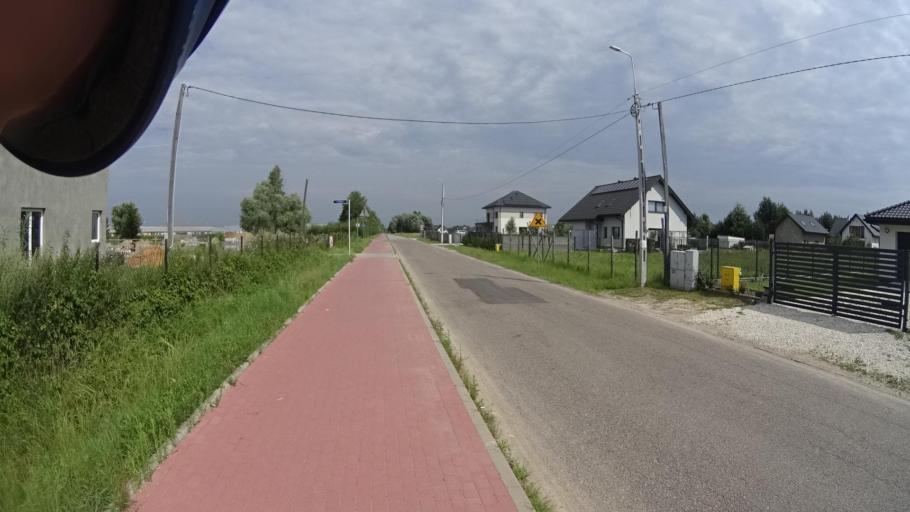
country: PL
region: Masovian Voivodeship
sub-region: Powiat pruszkowski
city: Nadarzyn
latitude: 52.0663
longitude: 20.7881
